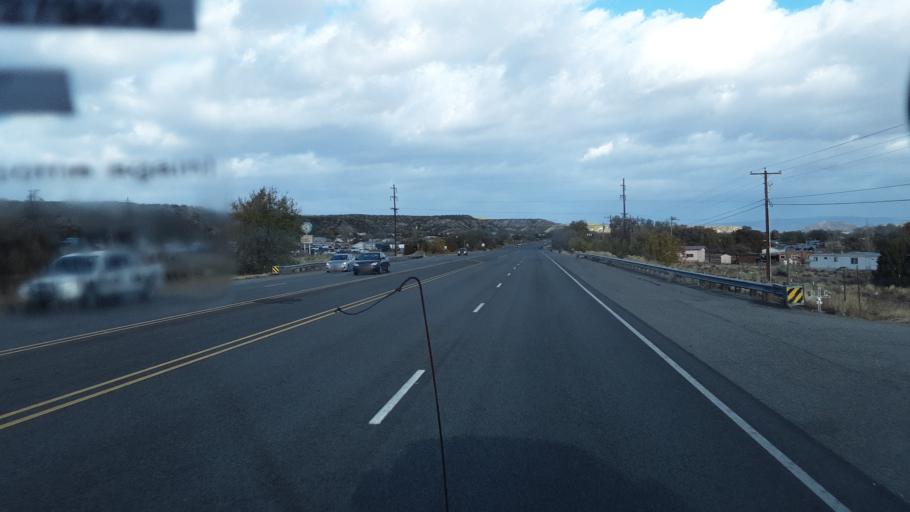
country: US
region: New Mexico
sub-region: Rio Arriba County
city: Ohkay Owingeh
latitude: 36.0458
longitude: -106.1072
